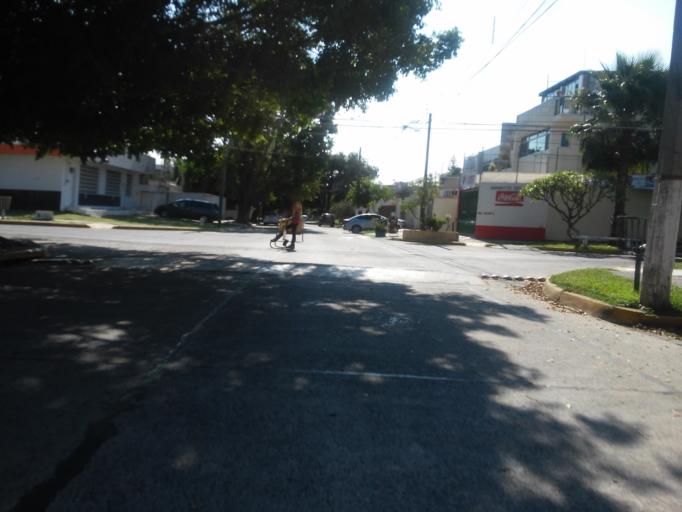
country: MX
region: Jalisco
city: Guadalajara
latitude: 20.6605
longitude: -103.4011
